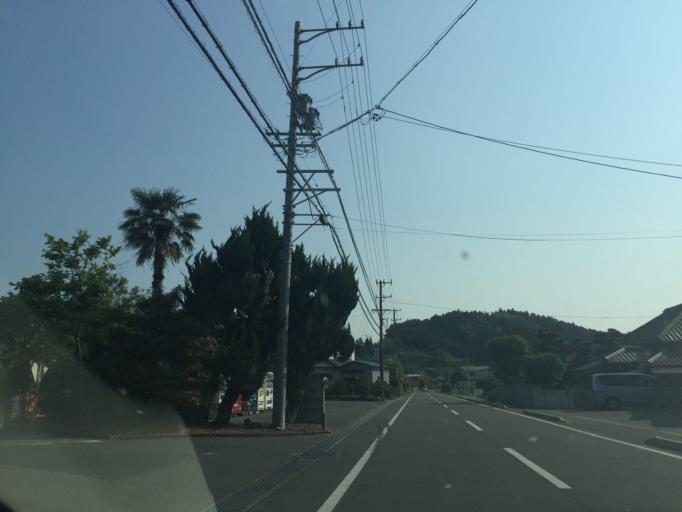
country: JP
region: Shizuoka
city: Kakegawa
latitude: 34.8131
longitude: 138.0347
